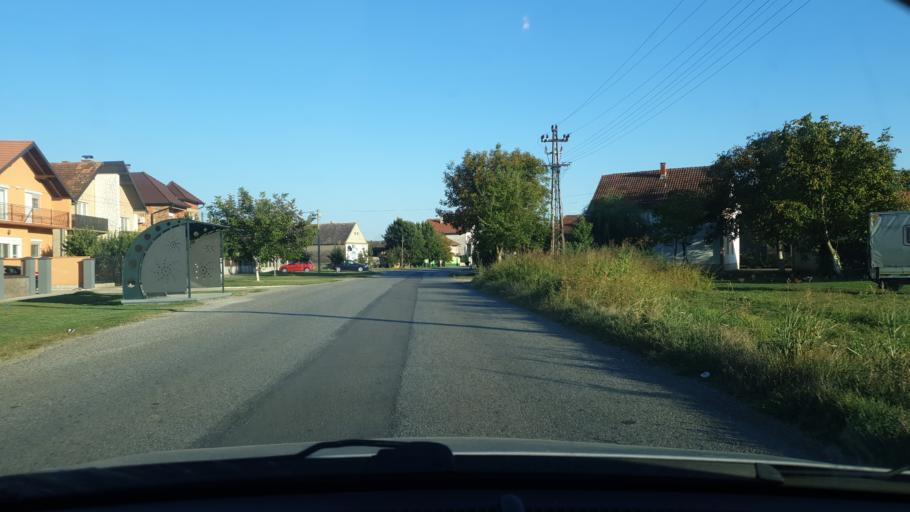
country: RS
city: Putinci
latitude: 44.9603
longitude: 19.9232
